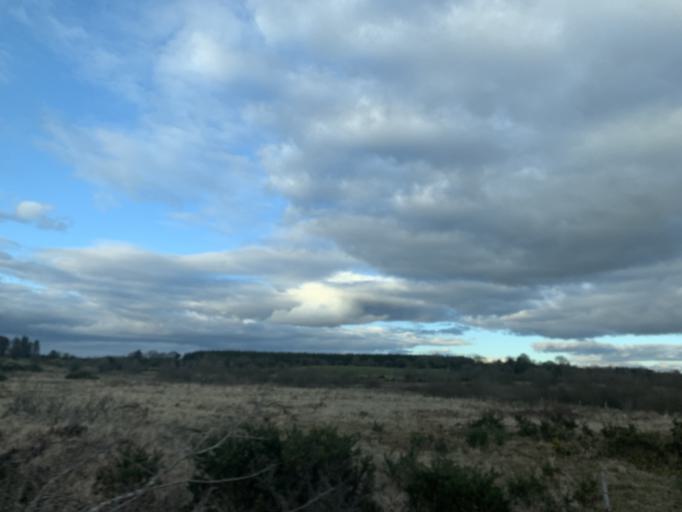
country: IE
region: Connaught
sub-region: Maigh Eo
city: Ballyhaunis
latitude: 53.8387
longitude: -8.7183
